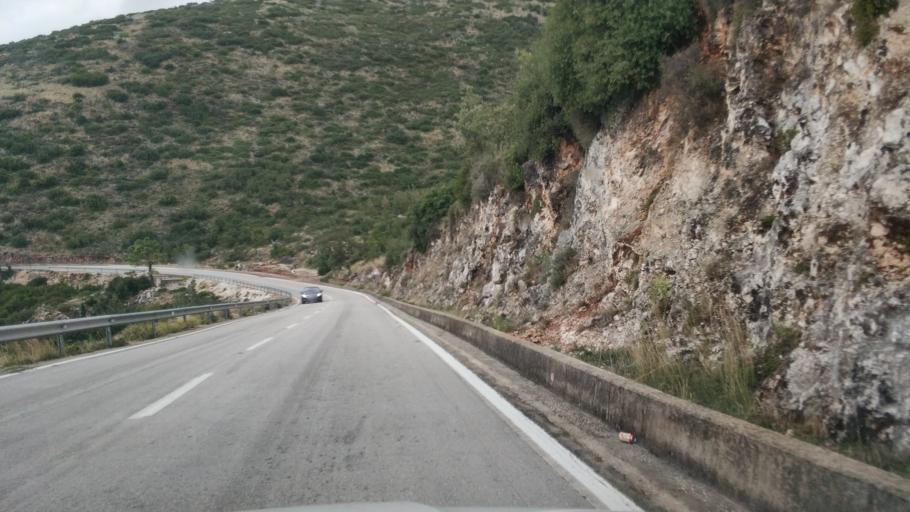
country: AL
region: Vlore
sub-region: Rrethi i Vlores
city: Vranisht
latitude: 40.1447
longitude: 19.6609
